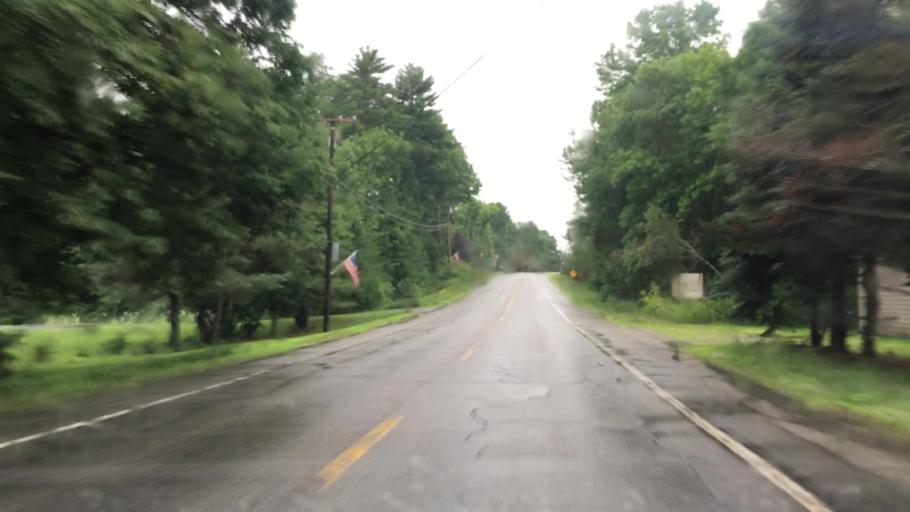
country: US
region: Maine
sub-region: Kennebec County
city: Pittston
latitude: 44.1921
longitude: -69.7588
